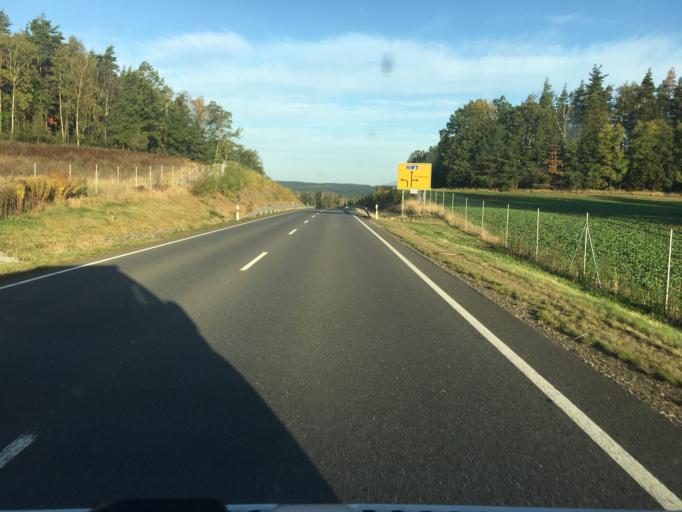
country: DE
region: Saxony
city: Kirchberg
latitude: 50.6137
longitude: 12.5058
